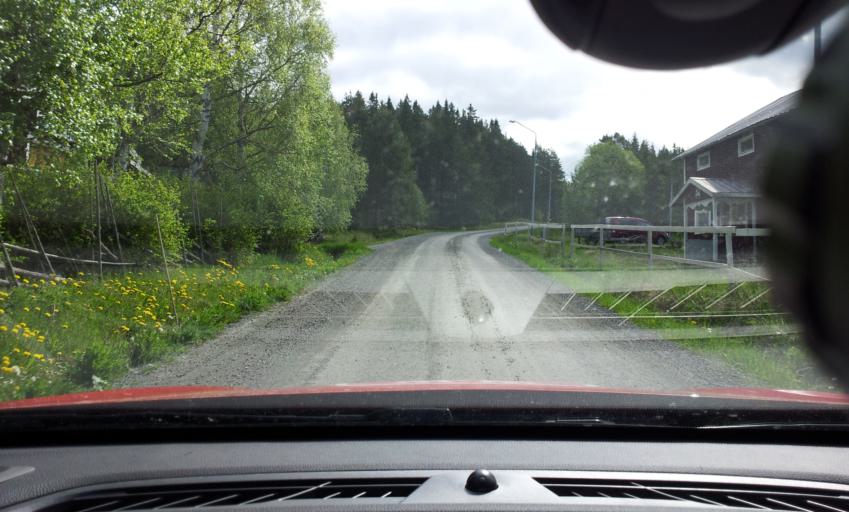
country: SE
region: Jaemtland
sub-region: OEstersunds Kommun
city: Ostersund
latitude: 63.1522
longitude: 14.5053
